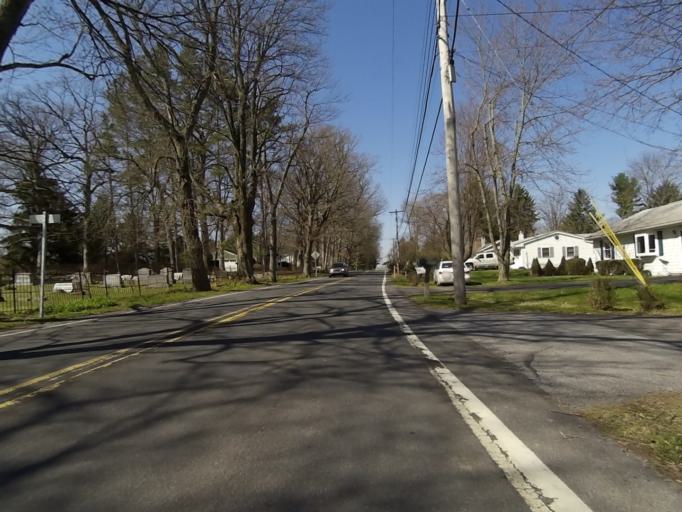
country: US
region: Pennsylvania
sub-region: Centre County
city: Pine Grove Mills
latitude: 40.7279
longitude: -77.9369
